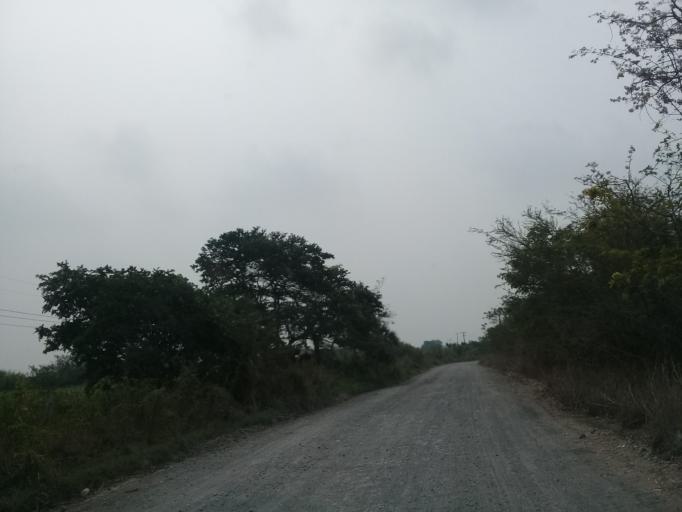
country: MX
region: Veracruz
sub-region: Medellin
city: La Laguna y Monte del Castillo
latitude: 18.9078
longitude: -96.1888
